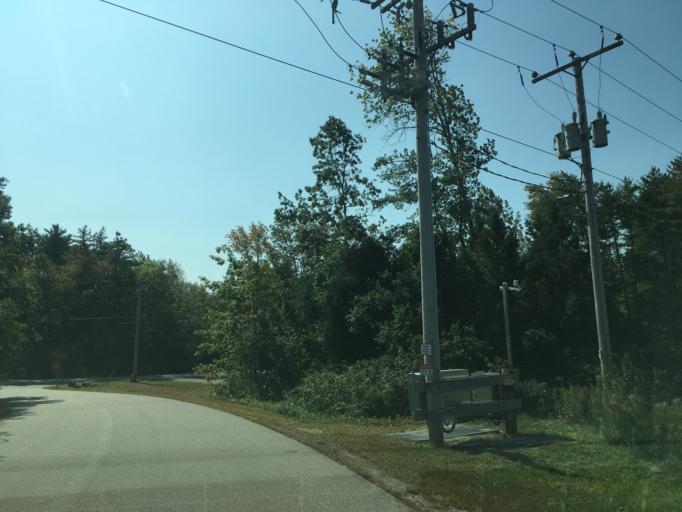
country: US
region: New Hampshire
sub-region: Rockingham County
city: Stratham Station
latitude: 43.0093
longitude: -70.8850
